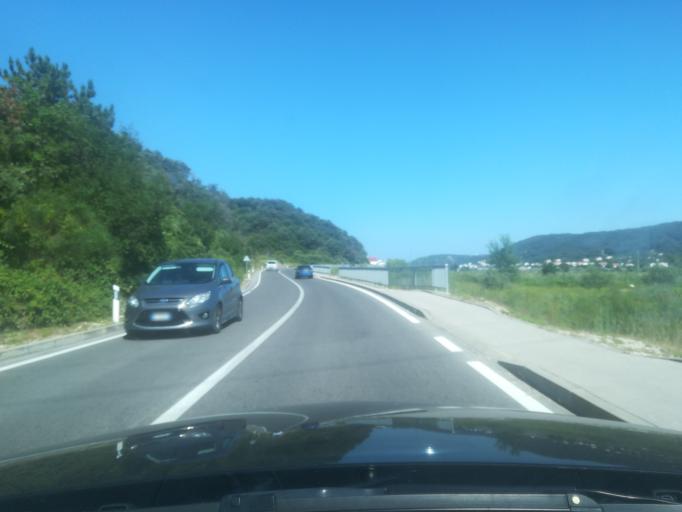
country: HR
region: Primorsko-Goranska
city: Supetarska Draga
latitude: 44.7904
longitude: 14.7354
